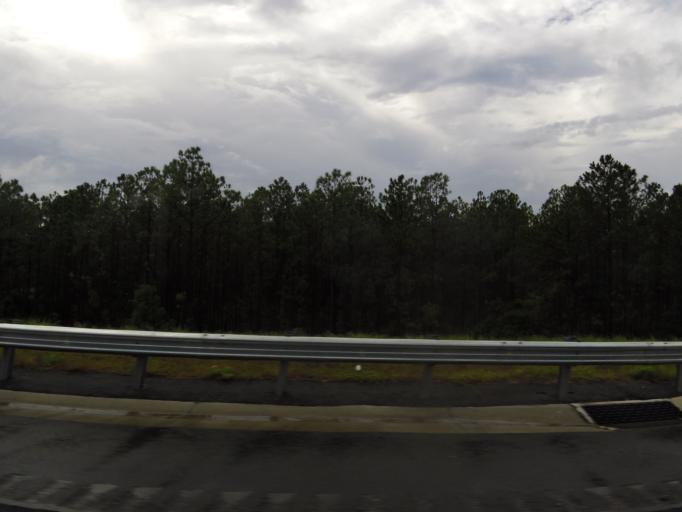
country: US
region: Florida
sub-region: Duval County
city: Baldwin
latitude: 30.3123
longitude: -81.8792
